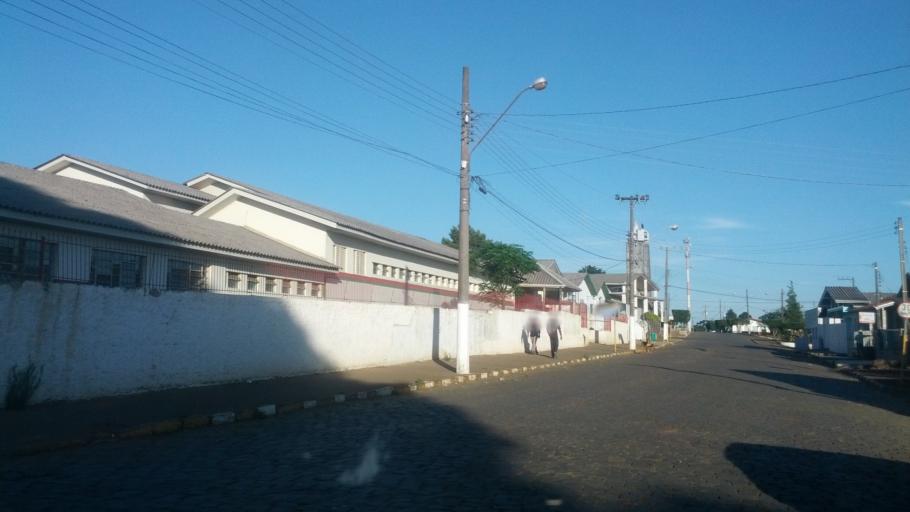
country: BR
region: Rio Grande do Sul
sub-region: Vacaria
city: Estrela
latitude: -27.9011
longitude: -50.7584
